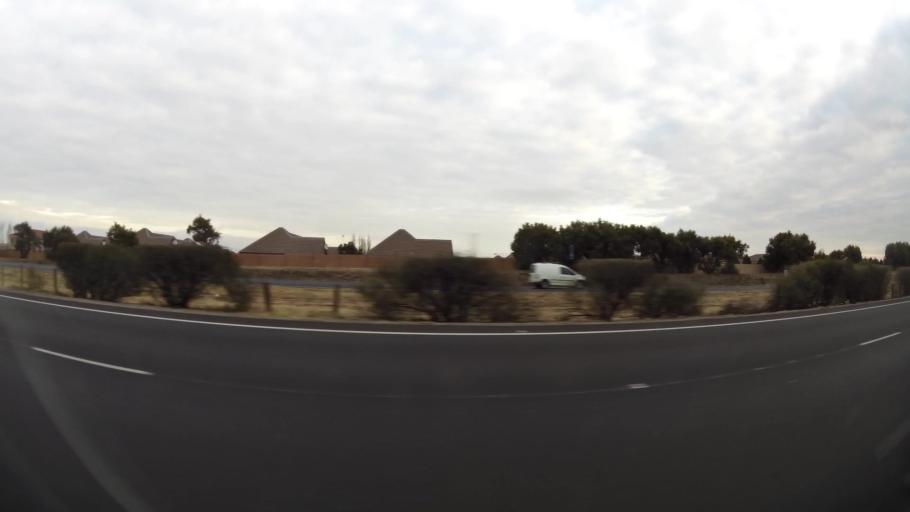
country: ZA
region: Orange Free State
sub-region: Mangaung Metropolitan Municipality
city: Bloemfontein
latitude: -29.0954
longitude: 26.1677
